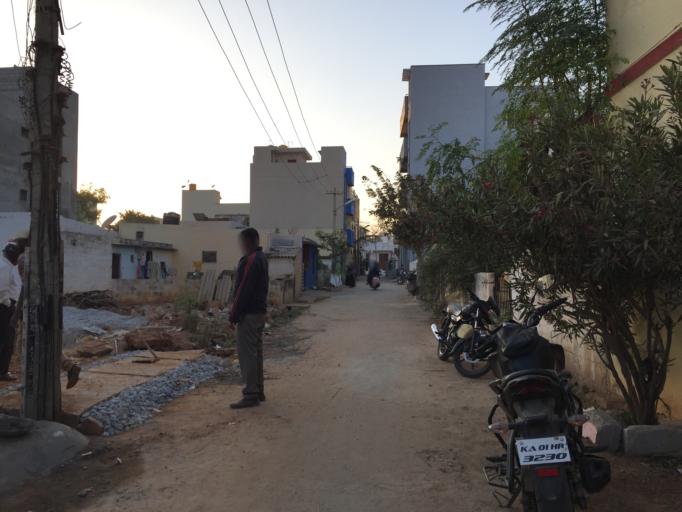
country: IN
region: Karnataka
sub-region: Bangalore Urban
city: Yelahanka
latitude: 13.0553
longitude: 77.6278
